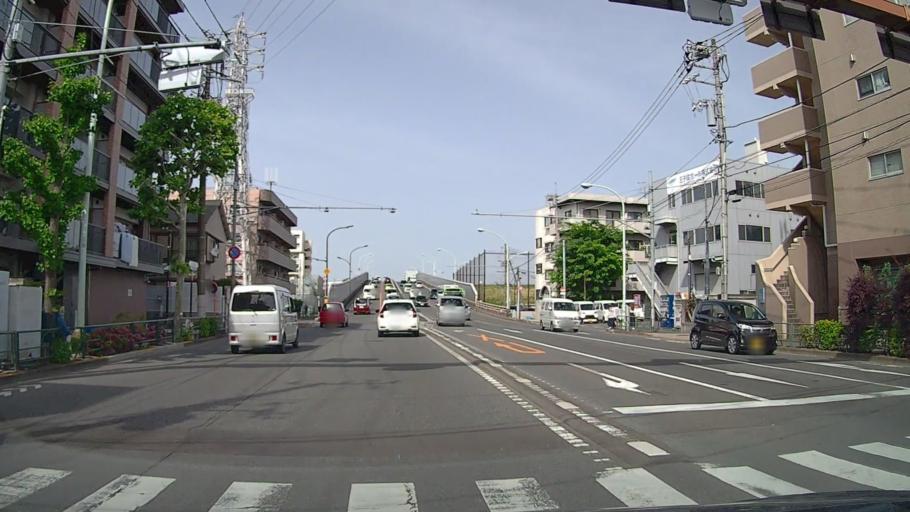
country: JP
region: Saitama
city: Kawaguchi
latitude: 35.7739
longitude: 139.7408
